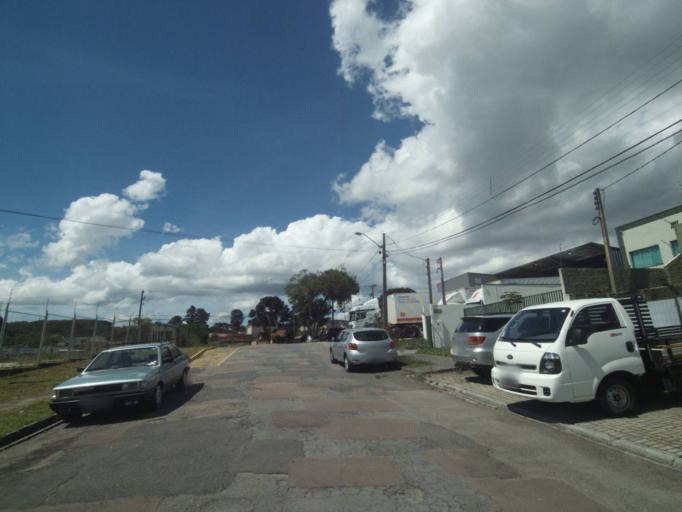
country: BR
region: Parana
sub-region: Curitiba
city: Curitiba
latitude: -25.4315
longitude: -49.3328
